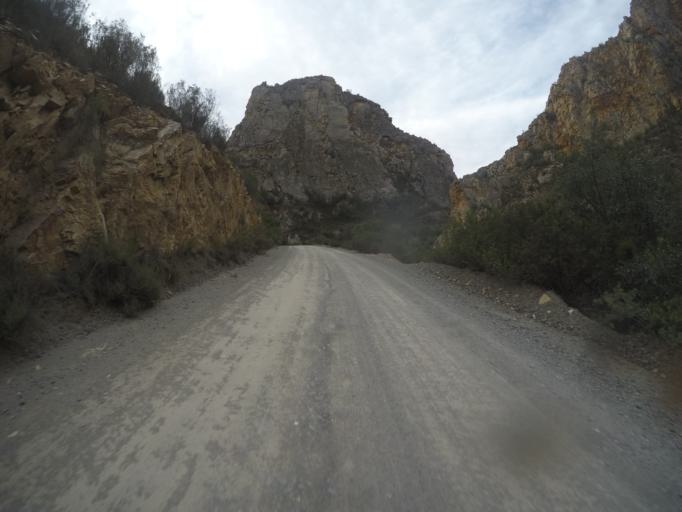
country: ZA
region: Eastern Cape
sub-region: Cacadu District Municipality
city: Willowmore
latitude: -33.5108
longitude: 23.6400
